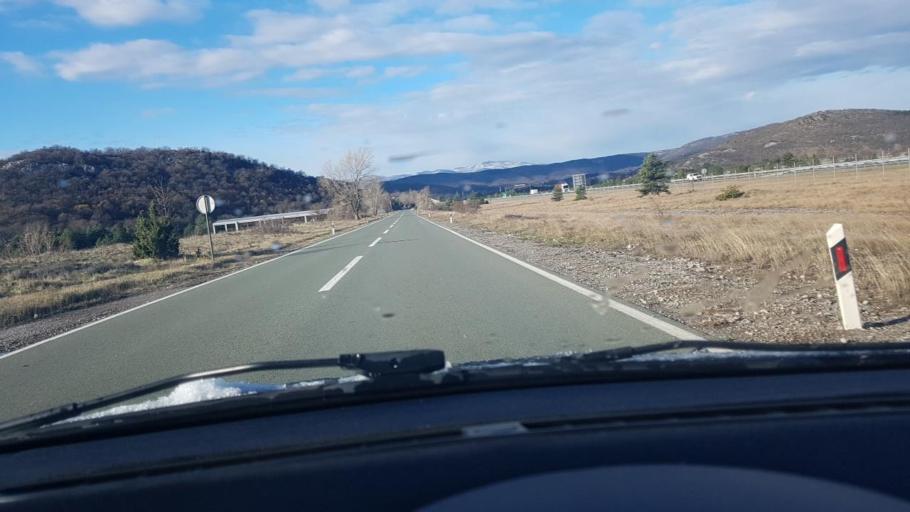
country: HR
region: Primorsko-Goranska
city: Podhum
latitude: 45.3760
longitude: 14.5108
